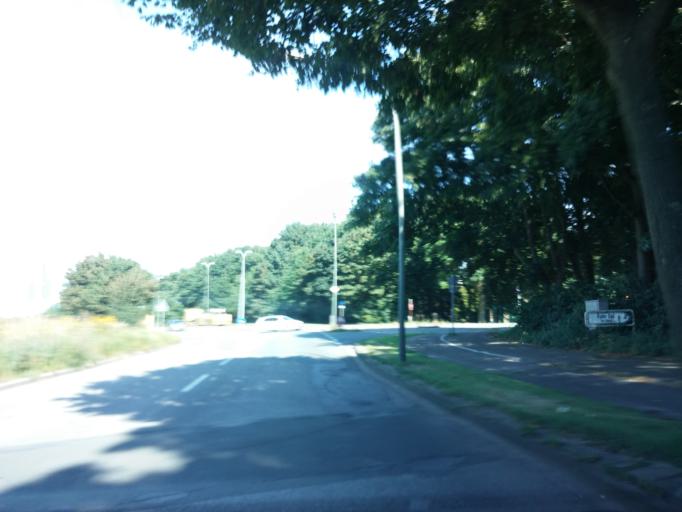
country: DE
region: North Rhine-Westphalia
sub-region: Regierungsbezirk Munster
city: Gladbeck
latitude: 51.6110
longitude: 7.0224
